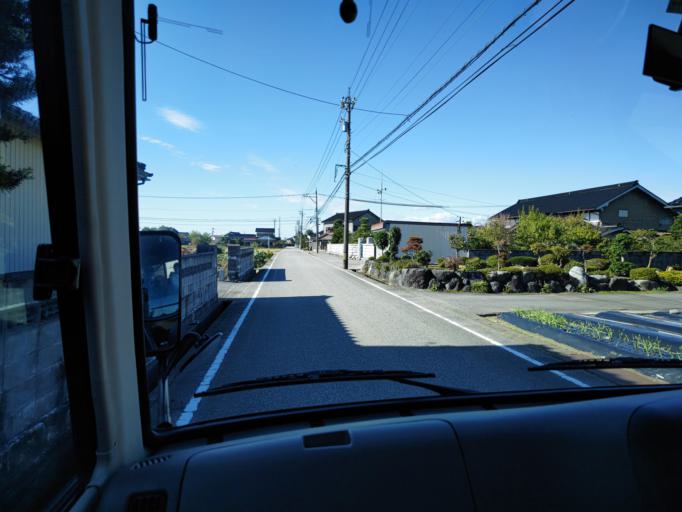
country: JP
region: Toyama
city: Nyuzen
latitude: 36.9105
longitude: 137.4324
